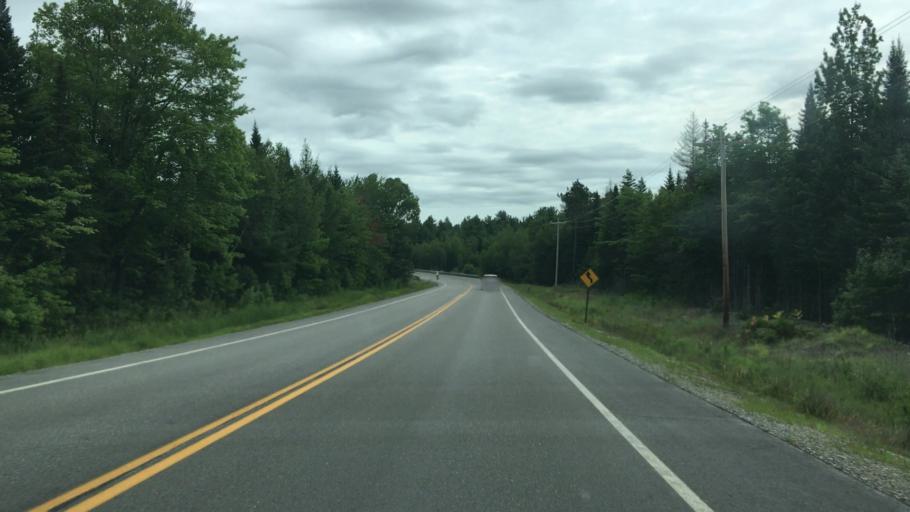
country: US
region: Maine
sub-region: Washington County
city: Machias
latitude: 44.9994
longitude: -67.5886
